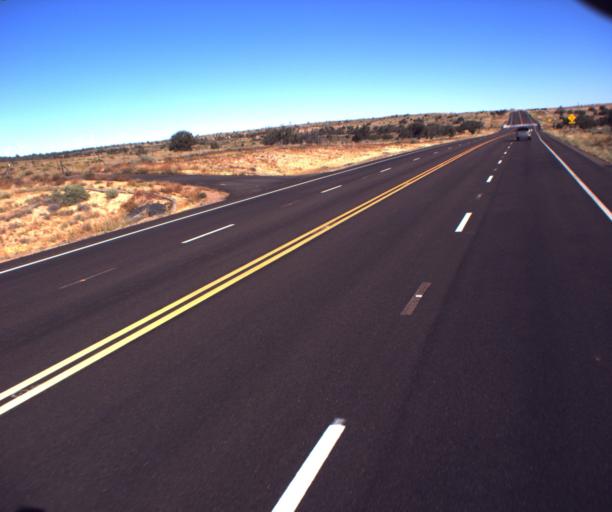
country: US
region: Arizona
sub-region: Navajo County
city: Snowflake
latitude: 34.5881
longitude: -110.0858
